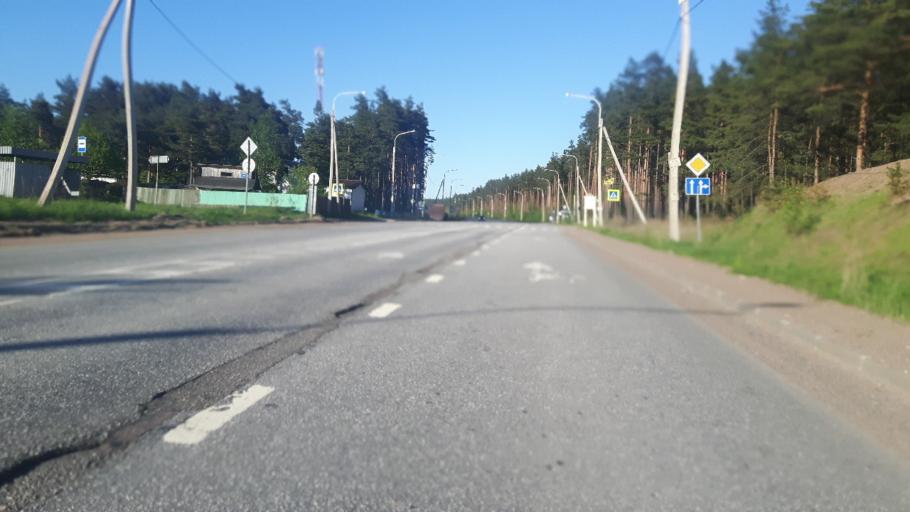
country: RU
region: Leningrad
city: Molodezhnoye
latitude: 60.1693
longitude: 29.4258
